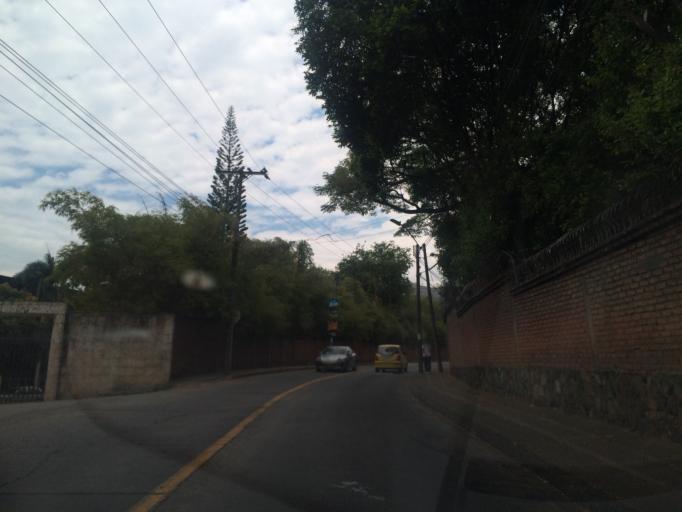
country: CO
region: Valle del Cauca
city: Cali
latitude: 3.4462
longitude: -76.5506
